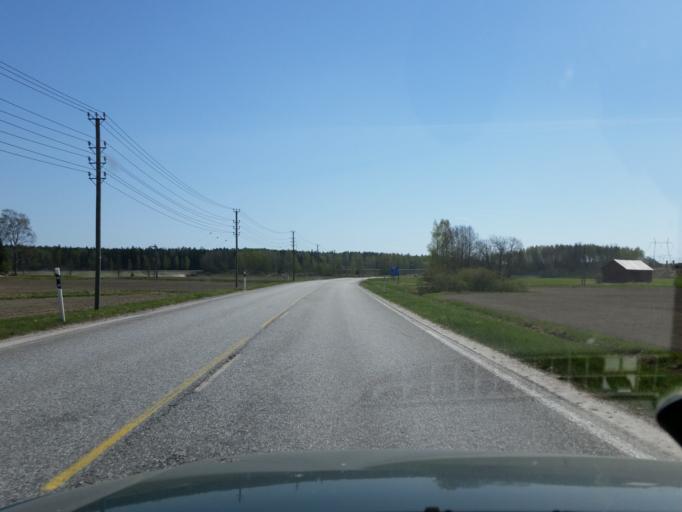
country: FI
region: Uusimaa
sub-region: Raaseporin
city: Inga
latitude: 60.0576
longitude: 23.9485
